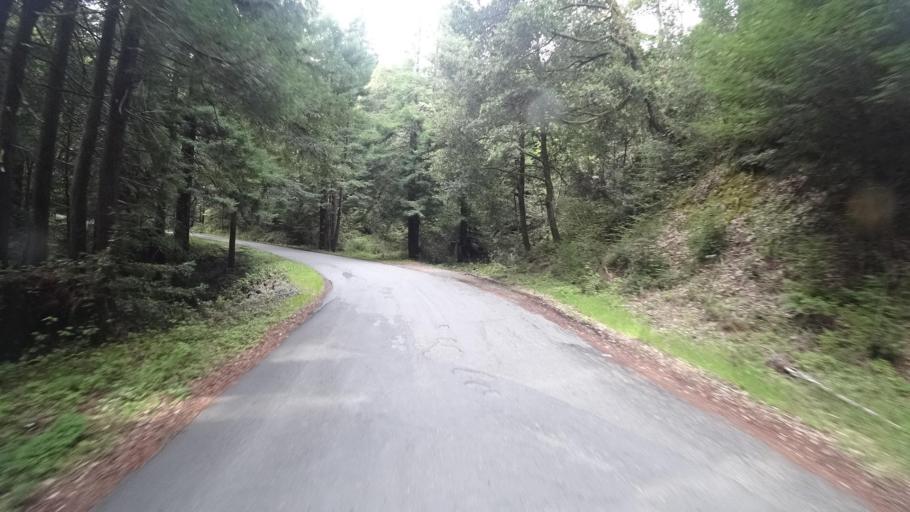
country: US
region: California
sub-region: Humboldt County
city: Redway
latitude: 40.3393
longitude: -123.9140
